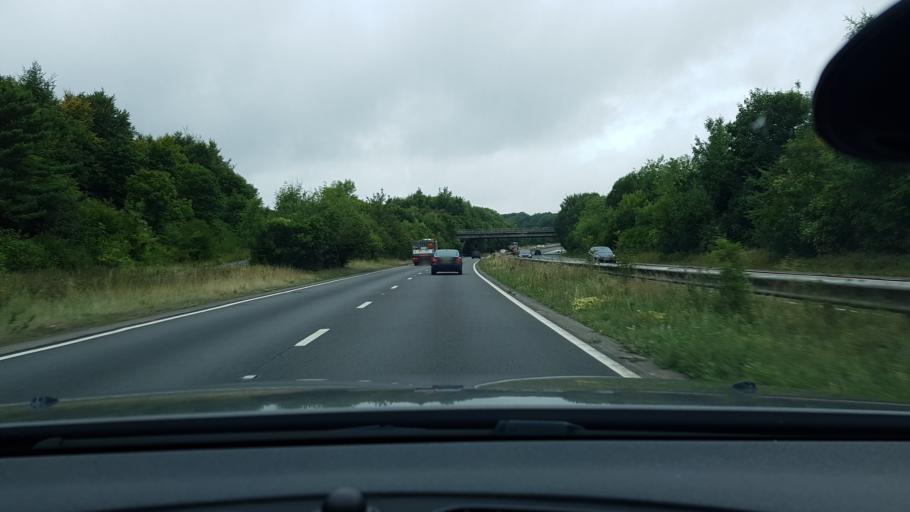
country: GB
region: England
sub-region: Hampshire
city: Winchester
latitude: 51.0998
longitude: -1.3377
